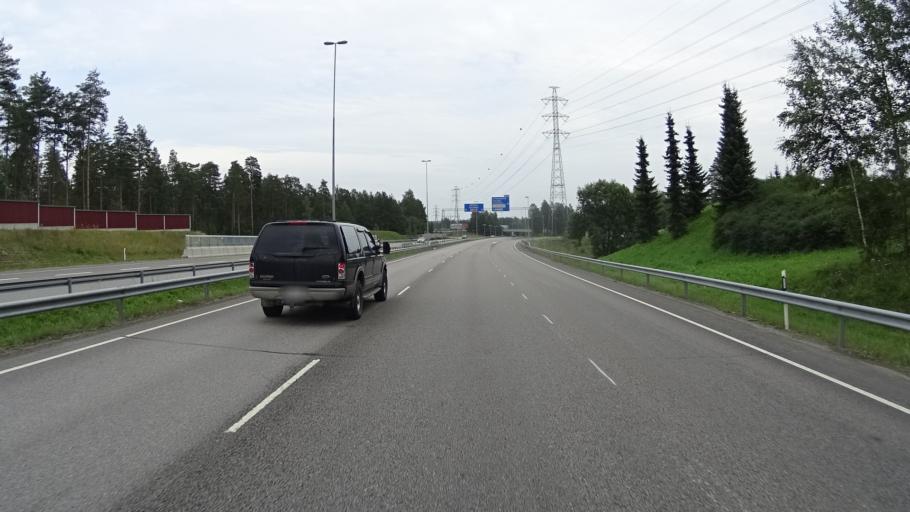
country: FI
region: South Karelia
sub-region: Lappeenranta
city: Lappeenranta
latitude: 61.0418
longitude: 28.1651
